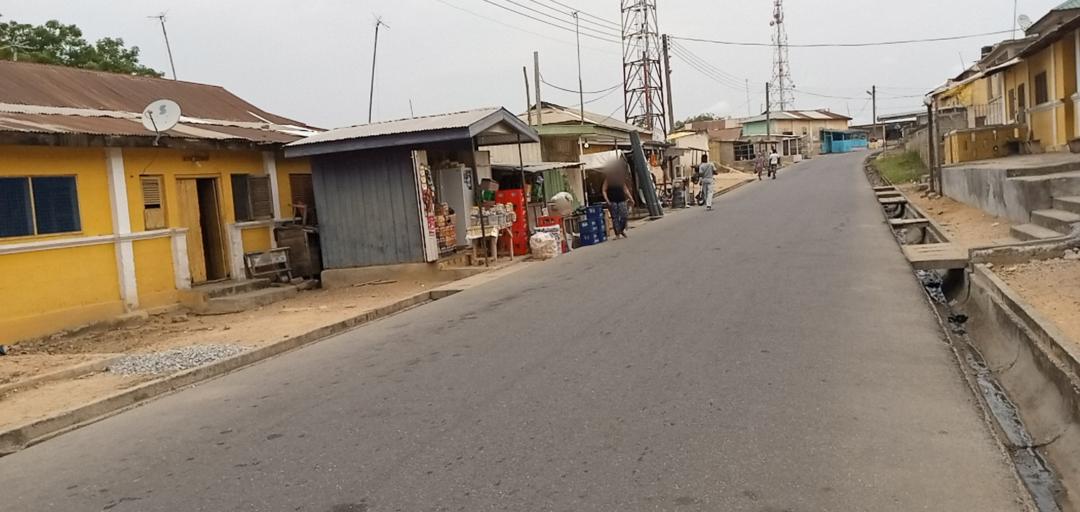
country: GH
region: Central
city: Winneba
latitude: 5.3481
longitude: -0.6268
